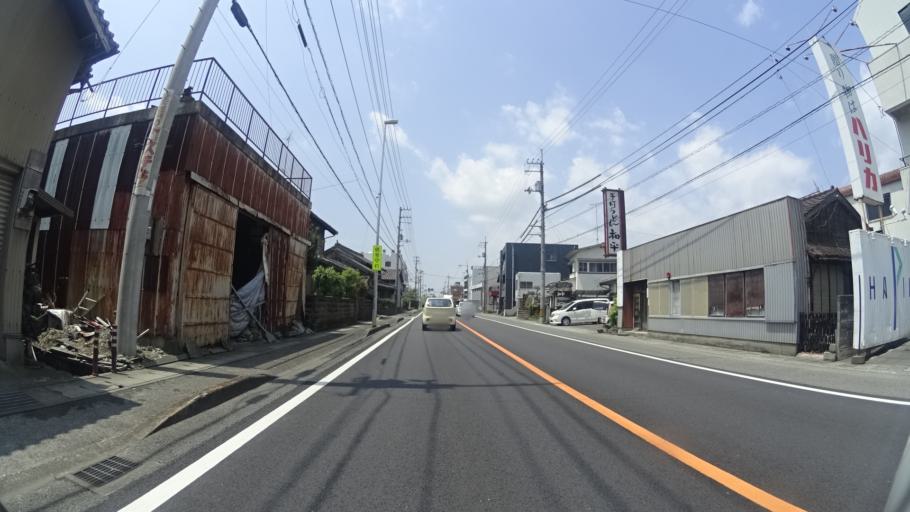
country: JP
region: Tokushima
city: Ishii
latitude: 34.0675
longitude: 134.4224
